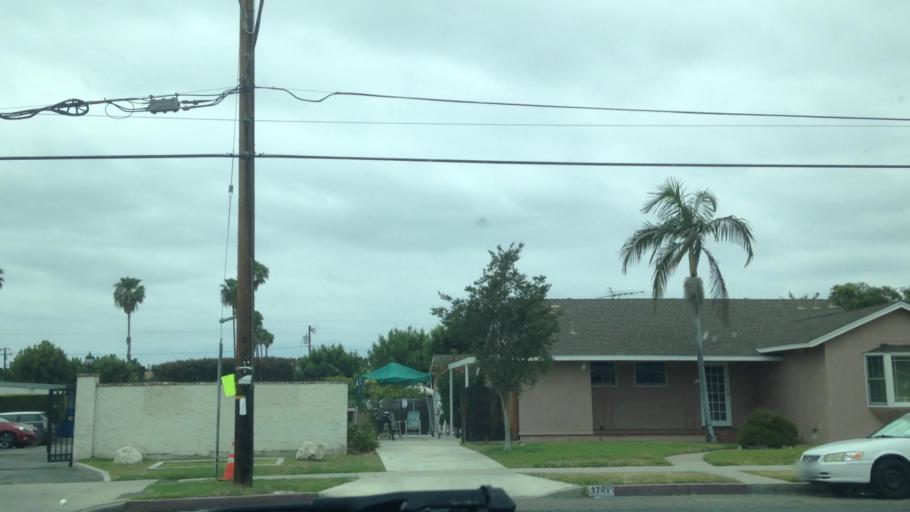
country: US
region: California
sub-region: Orange County
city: Anaheim
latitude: 33.8443
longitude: -117.8958
